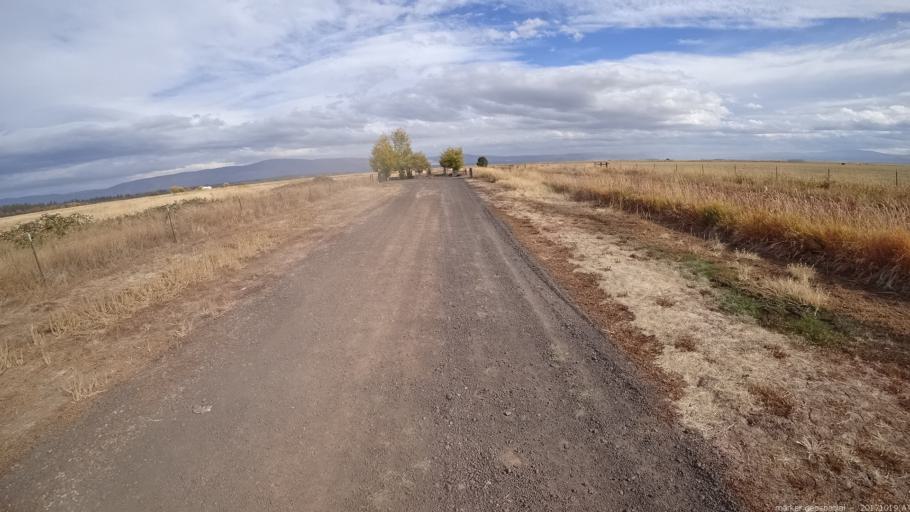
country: US
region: California
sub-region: Shasta County
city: Burney
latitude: 41.0979
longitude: -121.4716
